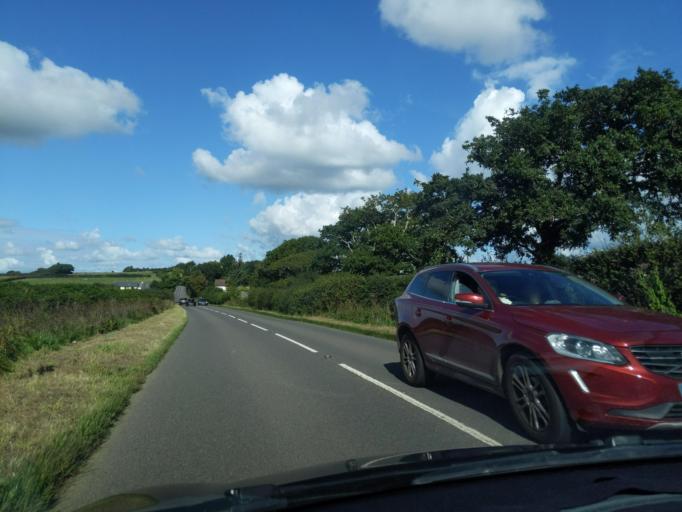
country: GB
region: England
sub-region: Cornwall
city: Werrington
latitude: 50.6706
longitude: -4.3263
